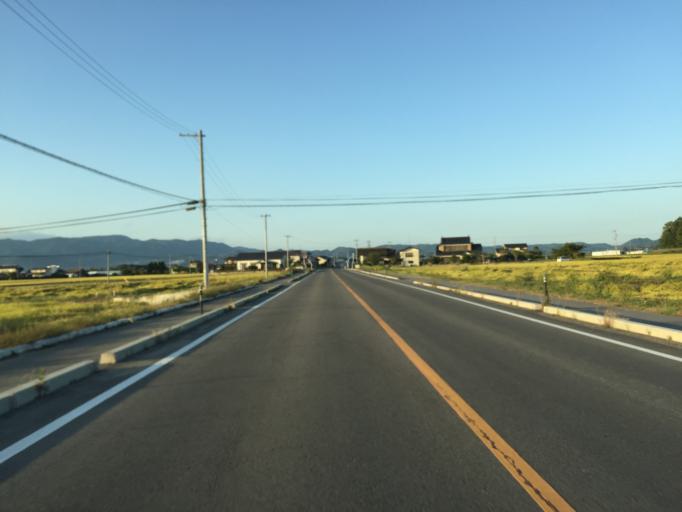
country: JP
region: Fukushima
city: Yanagawamachi-saiwaicho
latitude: 37.8290
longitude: 140.5928
